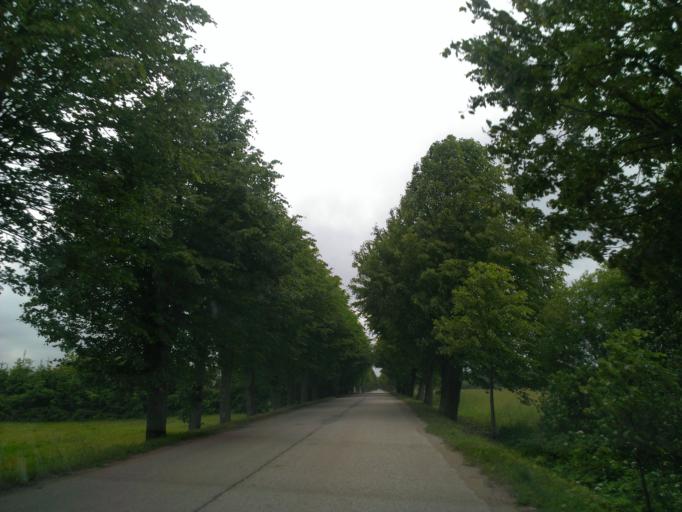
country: LV
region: Durbe
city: Liegi
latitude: 56.7299
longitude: 21.4026
